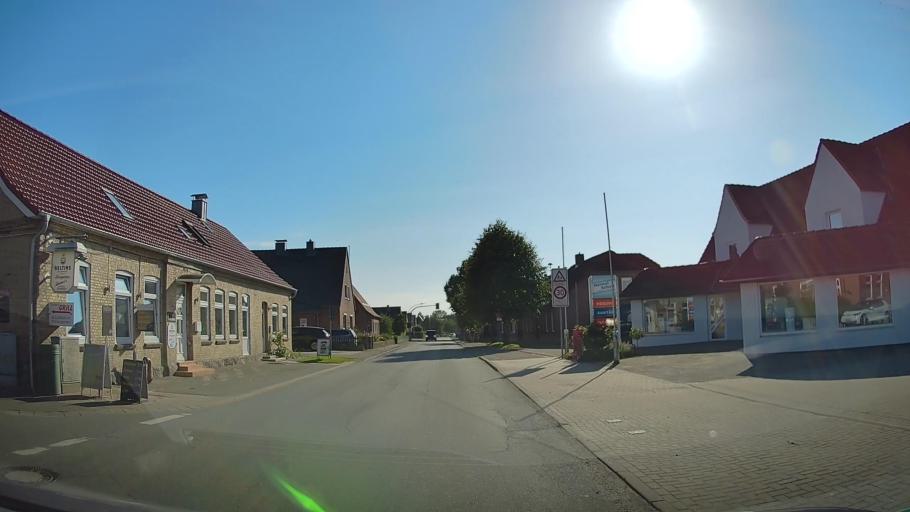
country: DE
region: Schleswig-Holstein
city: Fehmarn
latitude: 54.4496
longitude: 11.1450
